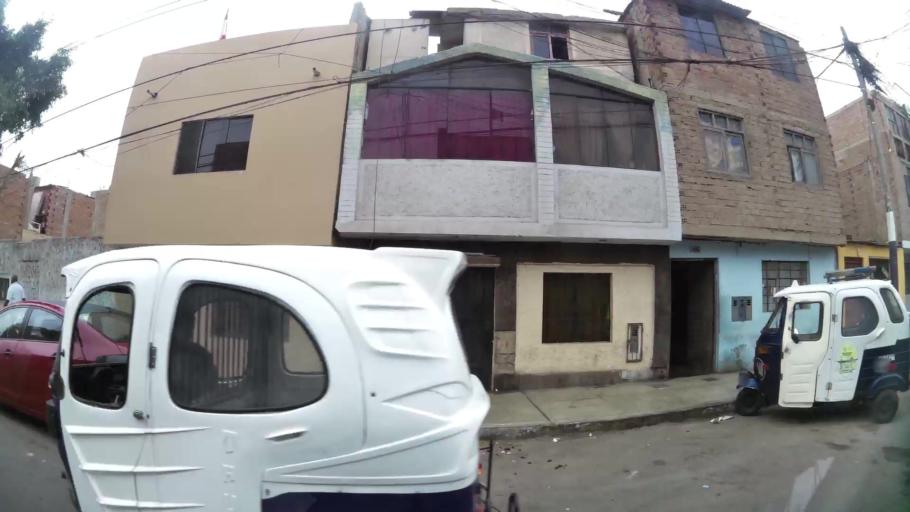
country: PE
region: Lima
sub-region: Lima
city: Surco
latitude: -12.1712
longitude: -77.0255
